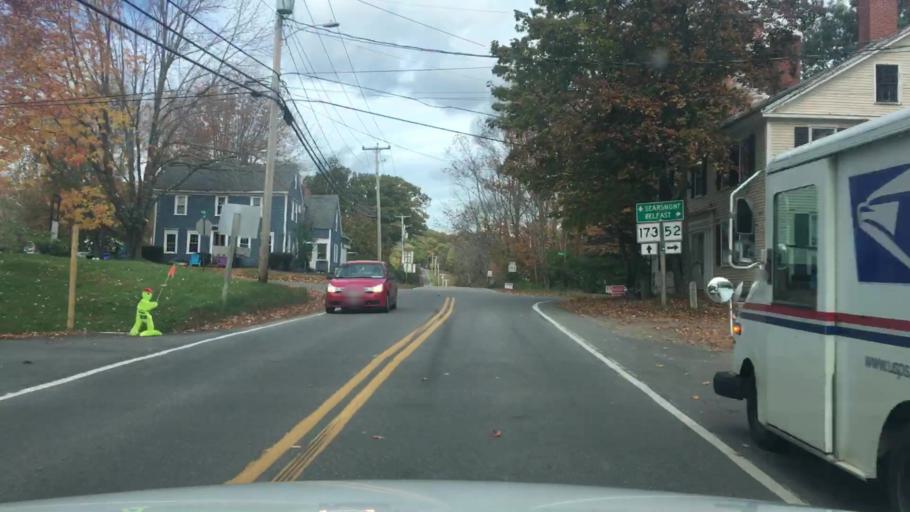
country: US
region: Maine
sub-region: Knox County
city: Hope
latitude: 44.2980
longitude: -69.1077
